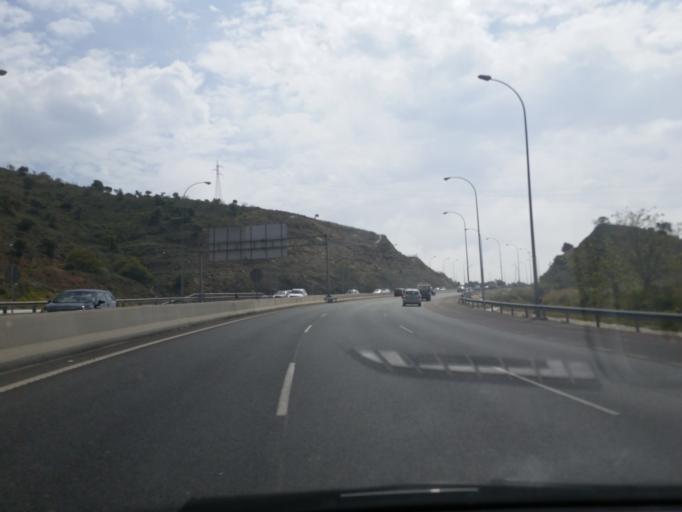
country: ES
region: Andalusia
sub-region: Provincia de Malaga
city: Malaga
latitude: 36.7554
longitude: -4.4171
